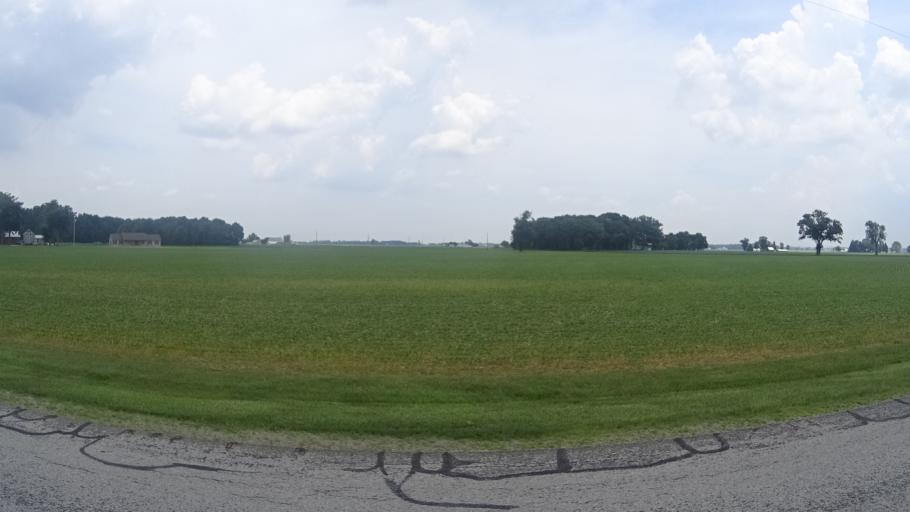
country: US
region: Ohio
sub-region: Erie County
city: Milan
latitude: 41.3141
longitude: -82.6691
